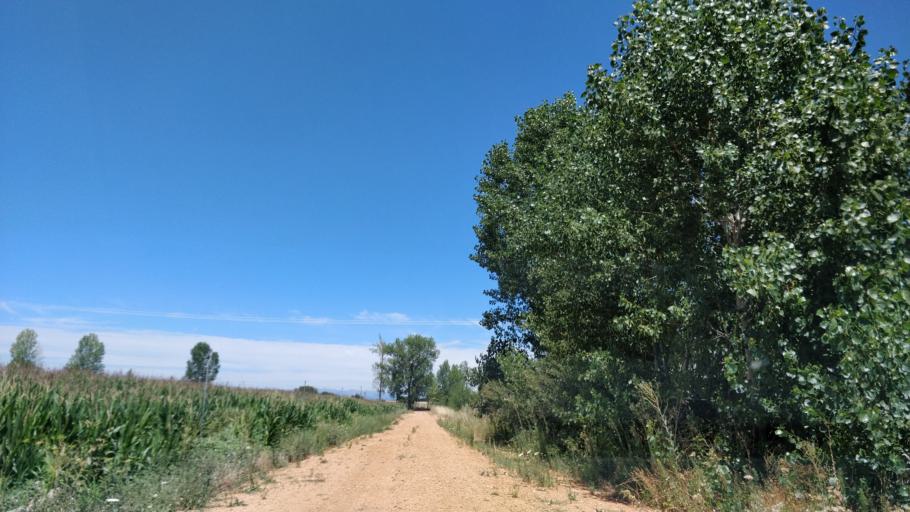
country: ES
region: Castille and Leon
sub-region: Provincia de Leon
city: Bustillo del Paramo
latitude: 42.4774
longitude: -5.8109
